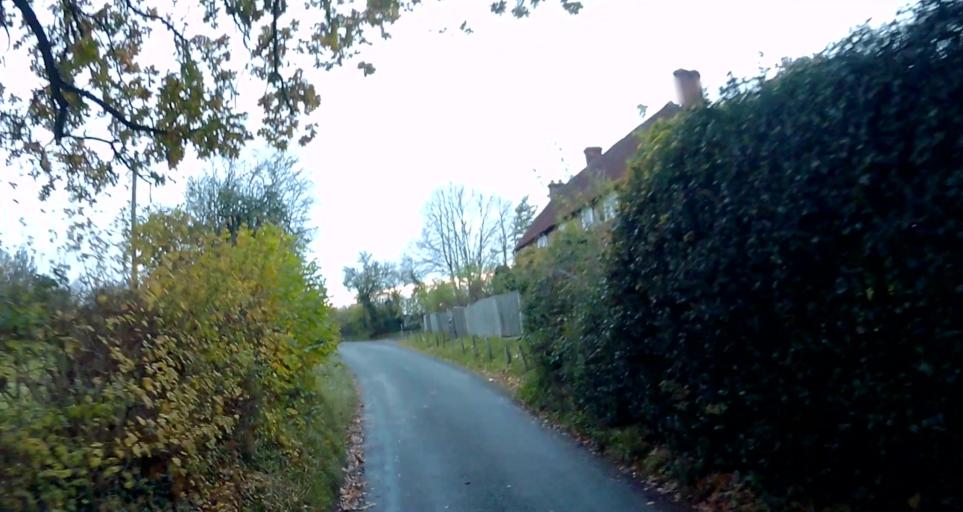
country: GB
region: England
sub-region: Hampshire
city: Odiham
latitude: 51.2507
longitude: -0.9216
